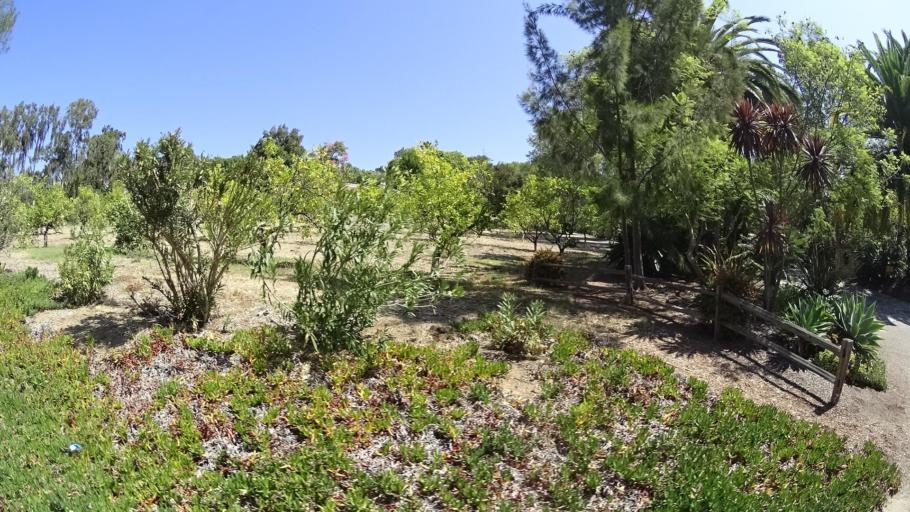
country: US
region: California
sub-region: San Diego County
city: Rancho Santa Fe
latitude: 33.0184
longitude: -117.1891
